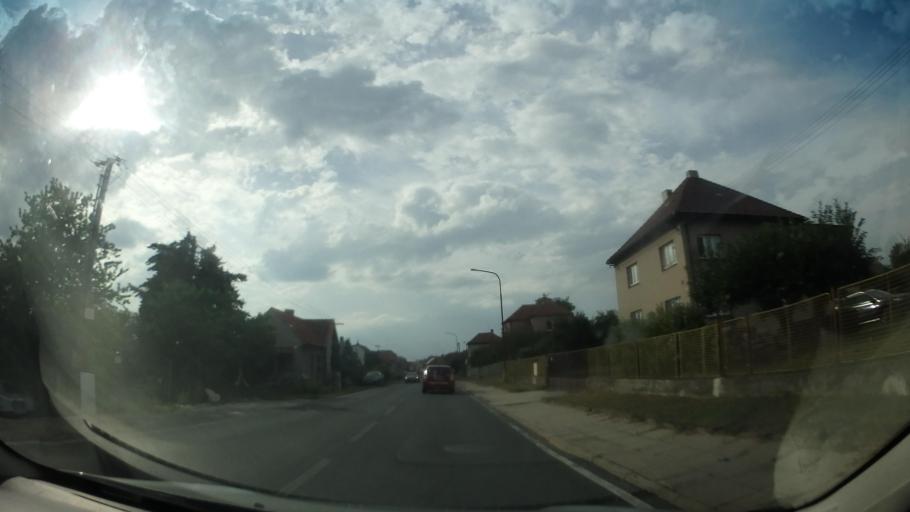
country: CZ
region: Pardubicky
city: Ronov nad Doubravou
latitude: 49.8862
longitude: 15.5404
